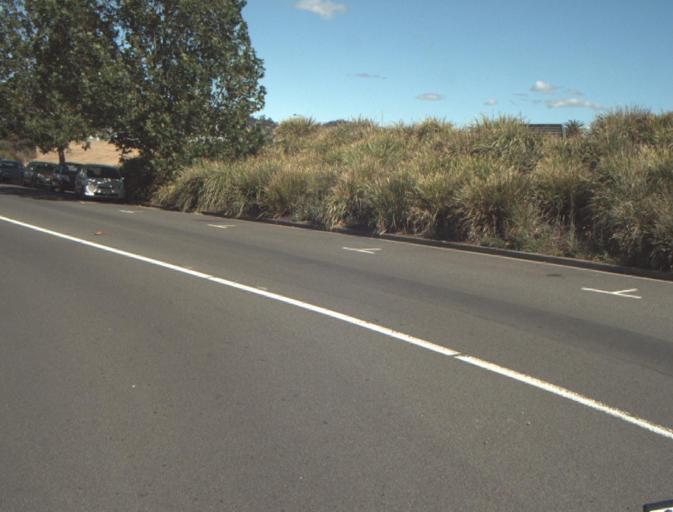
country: AU
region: Tasmania
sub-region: Launceston
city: Launceston
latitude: -41.4324
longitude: 147.1351
